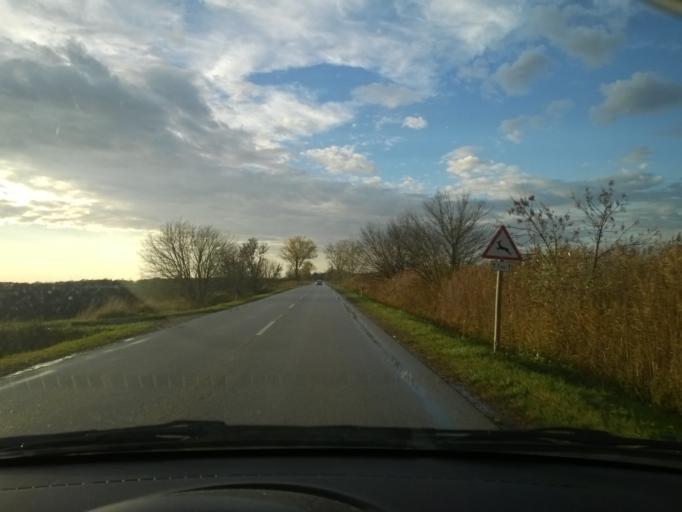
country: HU
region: Bacs-Kiskun
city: Kalocsa
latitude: 46.5098
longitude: 19.0224
